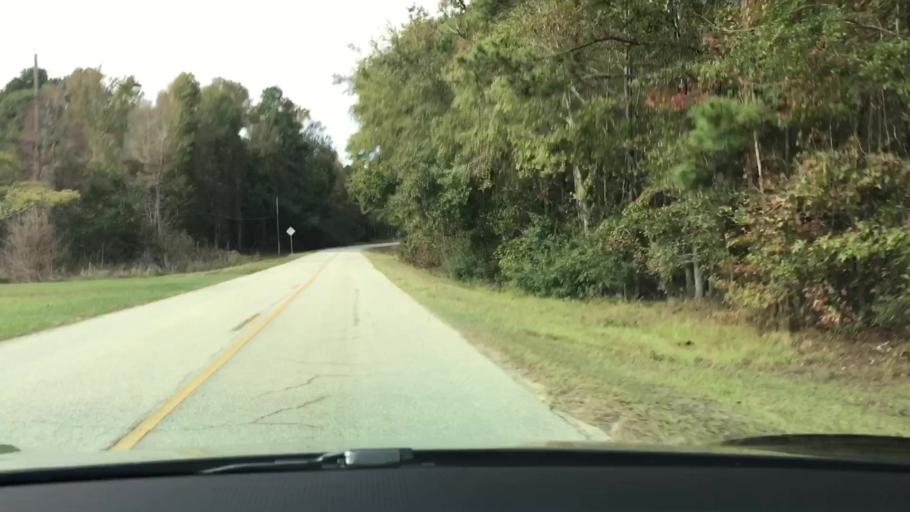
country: US
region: Georgia
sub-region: Jefferson County
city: Wadley
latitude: 32.7993
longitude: -82.3762
